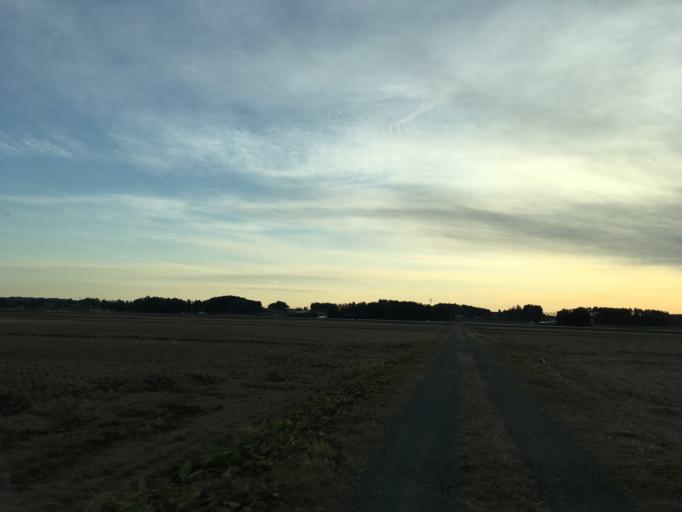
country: JP
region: Miyagi
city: Kogota
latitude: 38.6471
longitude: 141.0639
